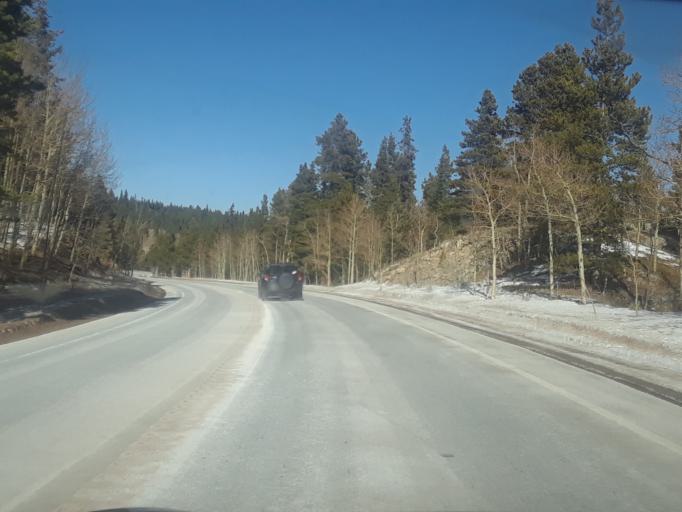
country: US
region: Colorado
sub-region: Boulder County
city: Nederland
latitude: 40.0877
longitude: -105.4961
